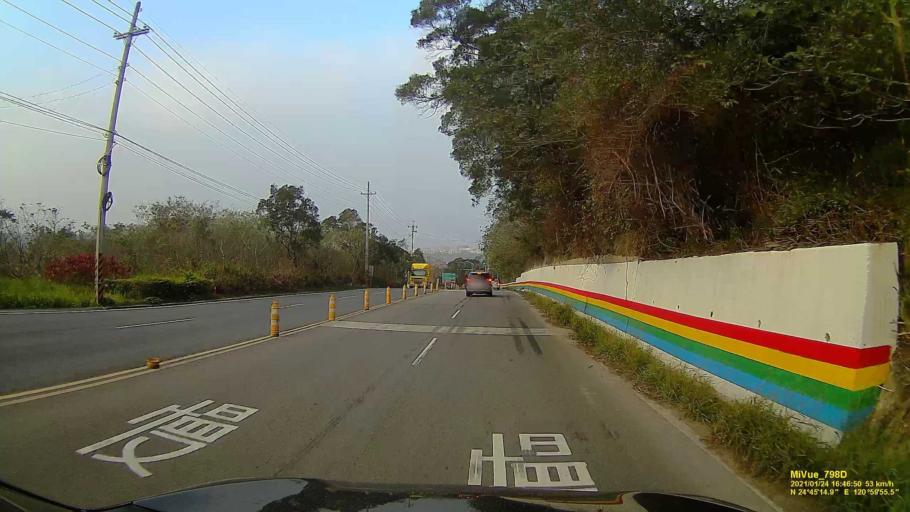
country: TW
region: Taiwan
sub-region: Hsinchu
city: Hsinchu
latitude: 24.7546
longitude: 120.9989
